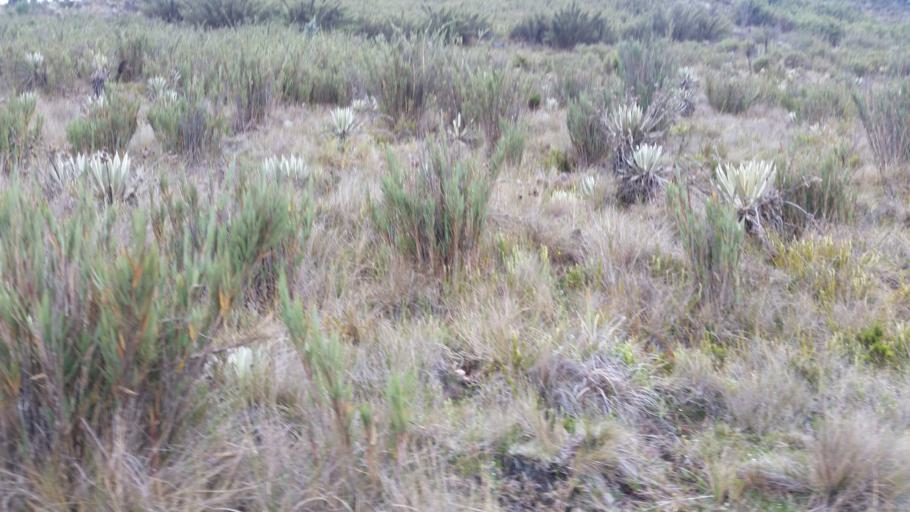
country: CO
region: Cundinamarca
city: Pasca
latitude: 4.3680
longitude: -74.2176
